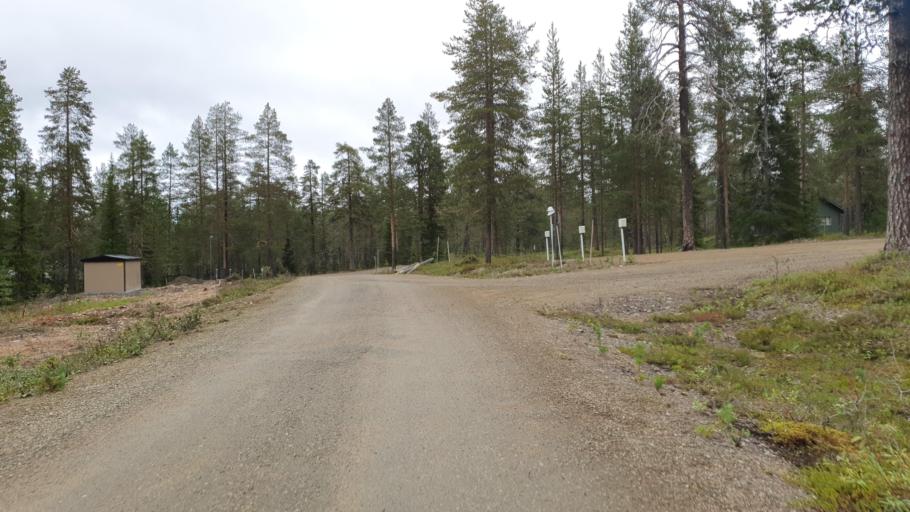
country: FI
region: Lapland
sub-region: Tunturi-Lappi
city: Kolari
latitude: 67.5974
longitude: 24.1849
